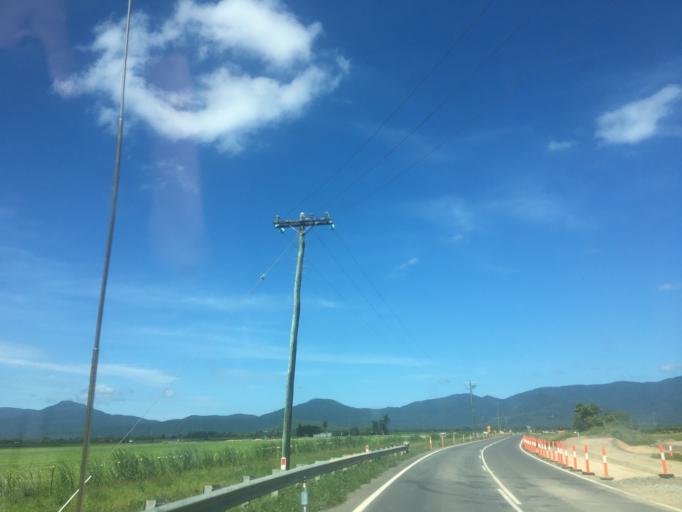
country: AU
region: Queensland
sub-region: Cairns
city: Woree
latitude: -17.0604
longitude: 145.7654
